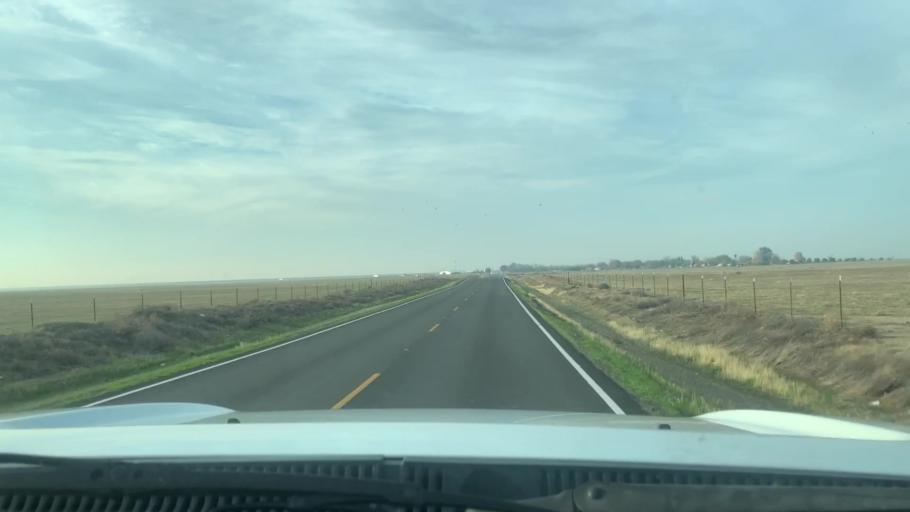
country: US
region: California
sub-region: Kern County
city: Lost Hills
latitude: 35.6036
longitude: -119.8538
